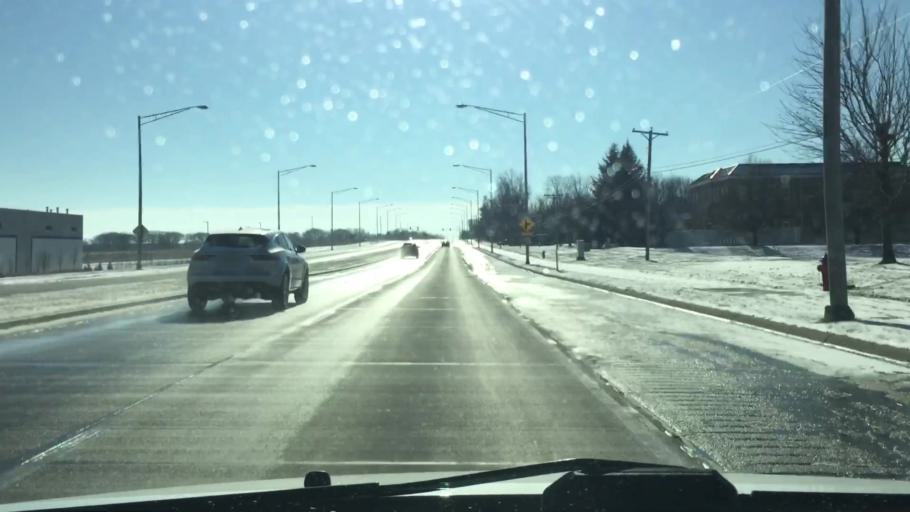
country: US
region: Illinois
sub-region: Kane County
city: Geneva
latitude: 41.9030
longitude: -88.2770
